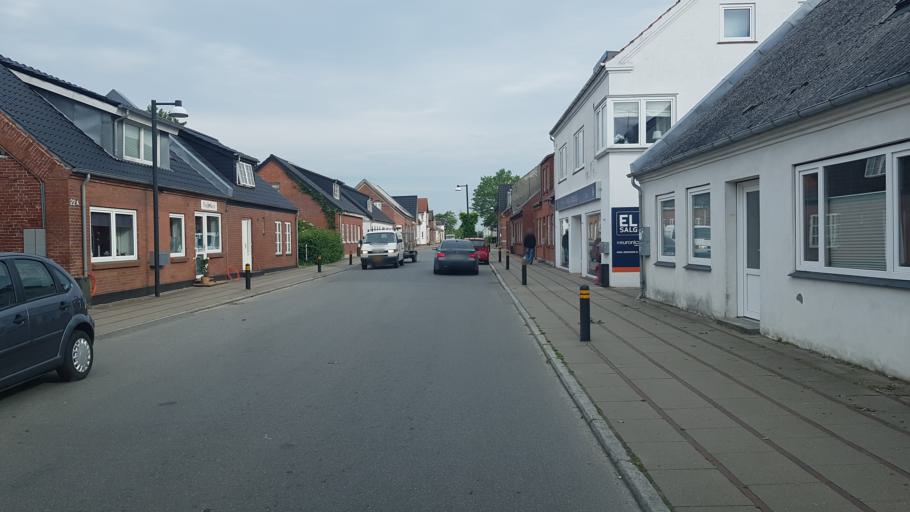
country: DK
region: South Denmark
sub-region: Esbjerg Kommune
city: Bramming
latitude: 55.4708
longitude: 8.8016
